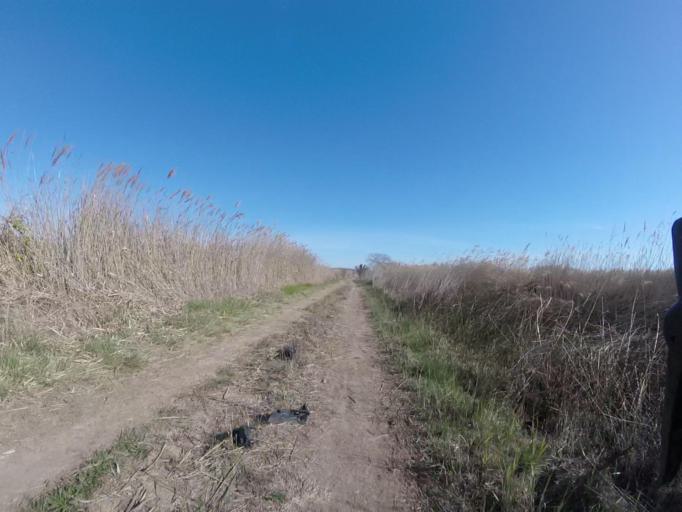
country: ES
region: Valencia
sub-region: Provincia de Castello
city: Torreblanca
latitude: 40.1668
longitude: 0.1730
